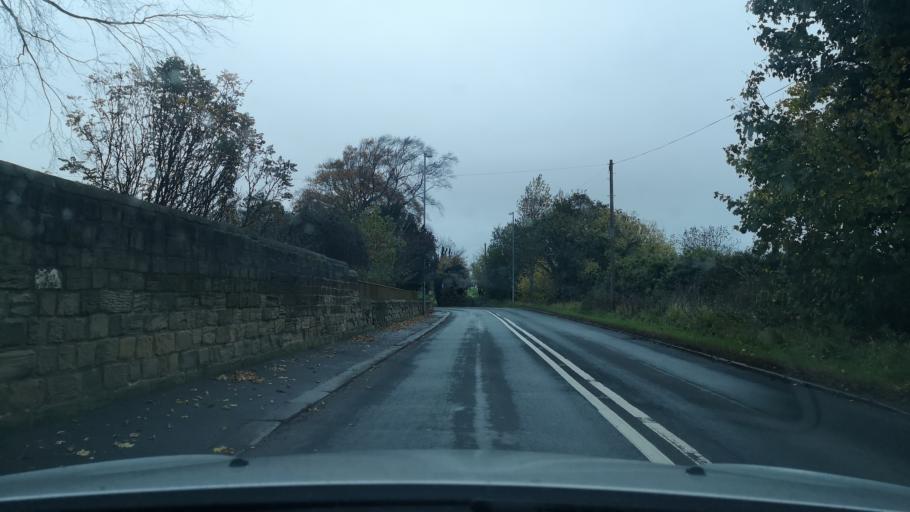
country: GB
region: England
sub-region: City and Borough of Wakefield
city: Low Ackworth
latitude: 53.6608
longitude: -1.3281
